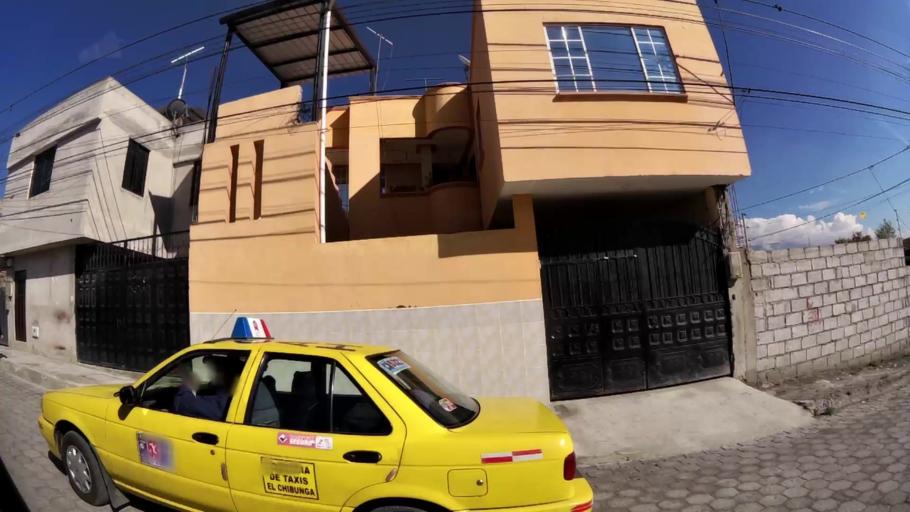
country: EC
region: Chimborazo
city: Riobamba
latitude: -1.6512
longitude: -78.6733
